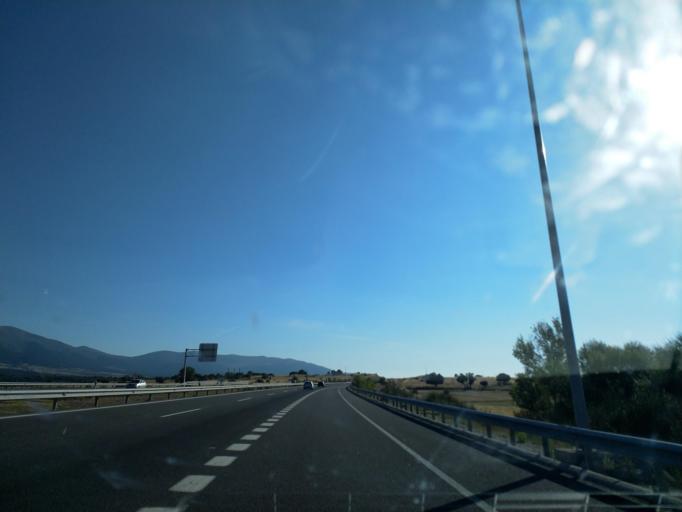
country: ES
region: Castille and Leon
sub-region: Provincia de Segovia
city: Segovia
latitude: 40.9001
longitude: -4.1059
